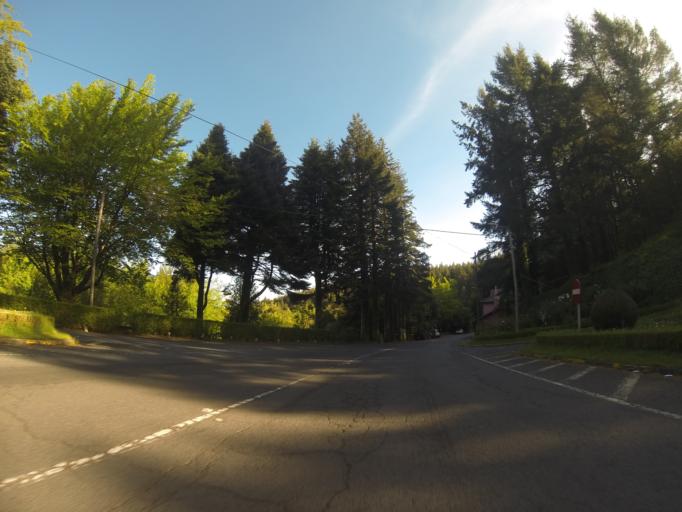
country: PT
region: Madeira
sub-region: Funchal
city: Nossa Senhora do Monte
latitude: 32.7097
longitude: -16.8876
